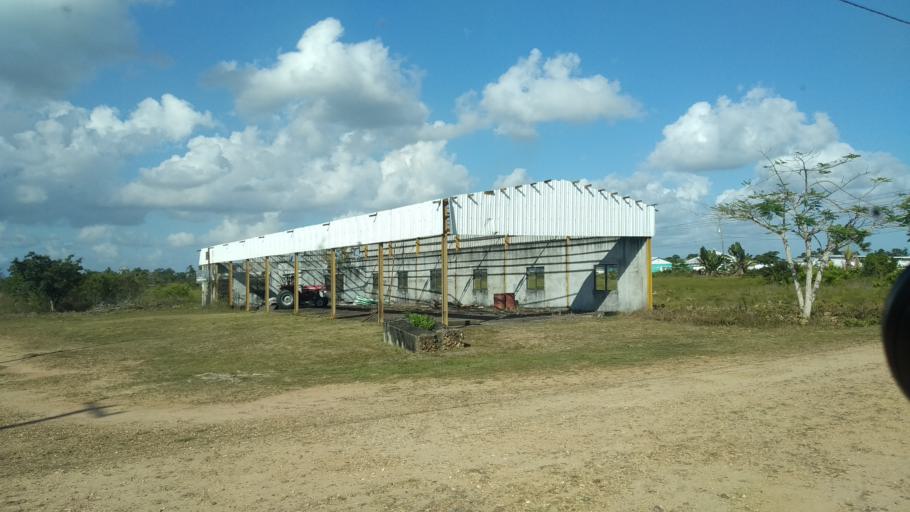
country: BZ
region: Cayo
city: Belmopan
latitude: 17.3937
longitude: -88.5123
